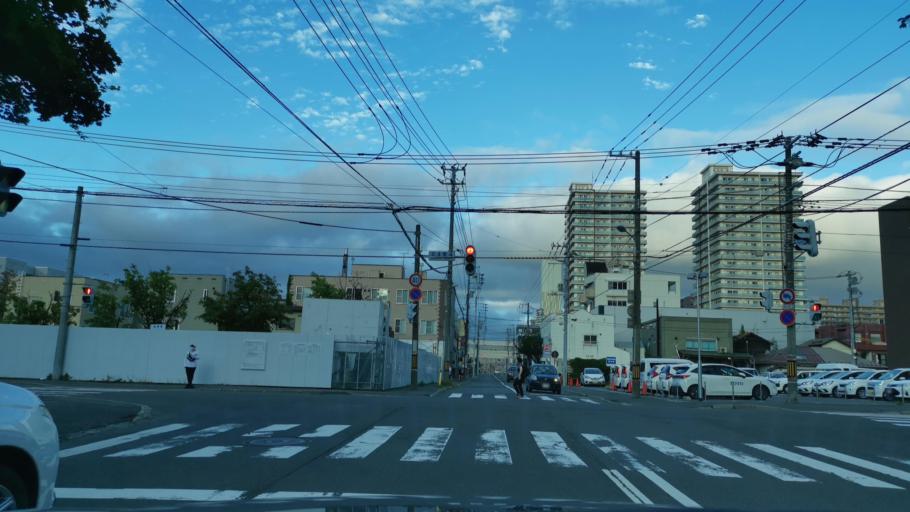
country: JP
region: Hokkaido
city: Sapporo
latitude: 43.0669
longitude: 141.3603
